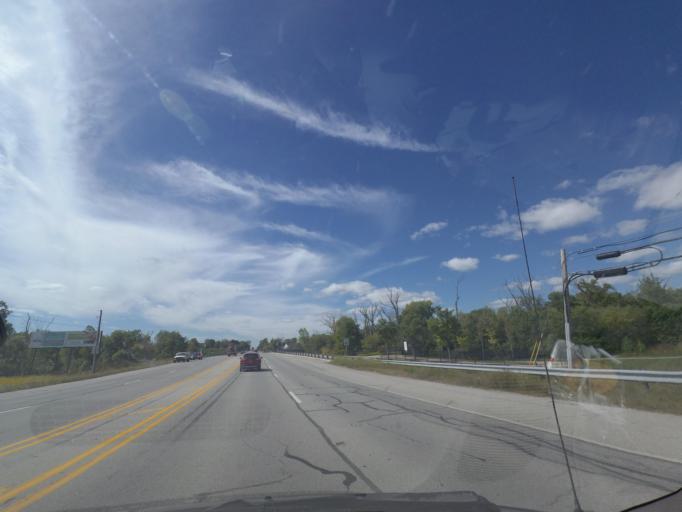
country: US
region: Indiana
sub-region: Marion County
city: Cumberland
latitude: 39.7770
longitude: -85.9464
